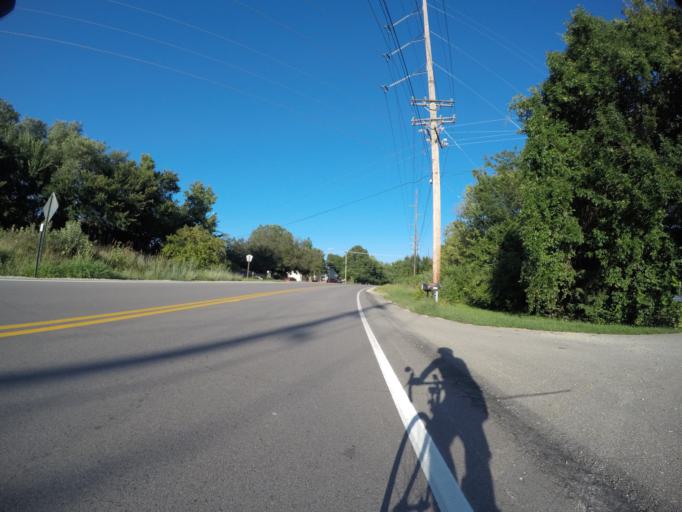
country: US
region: Kansas
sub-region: Riley County
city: Manhattan
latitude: 39.1599
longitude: -96.6122
